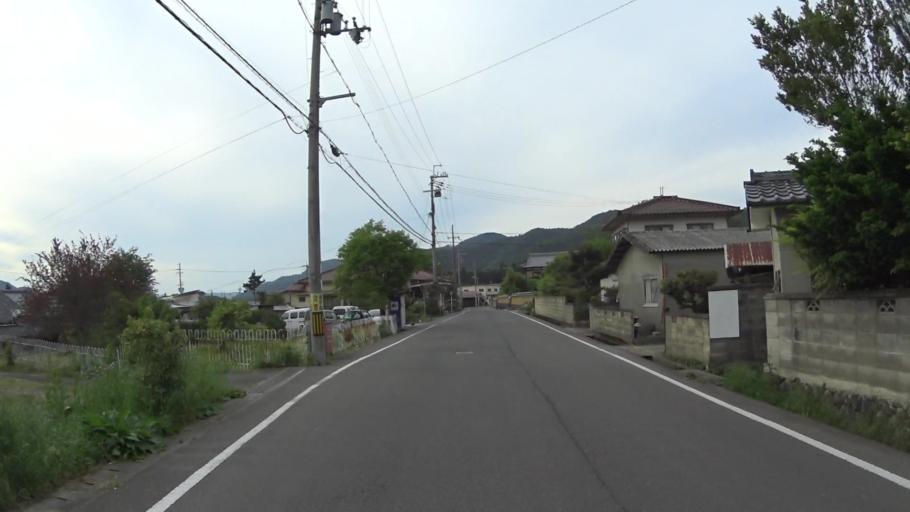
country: JP
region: Kyoto
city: Kameoka
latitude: 35.0859
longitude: 135.5633
